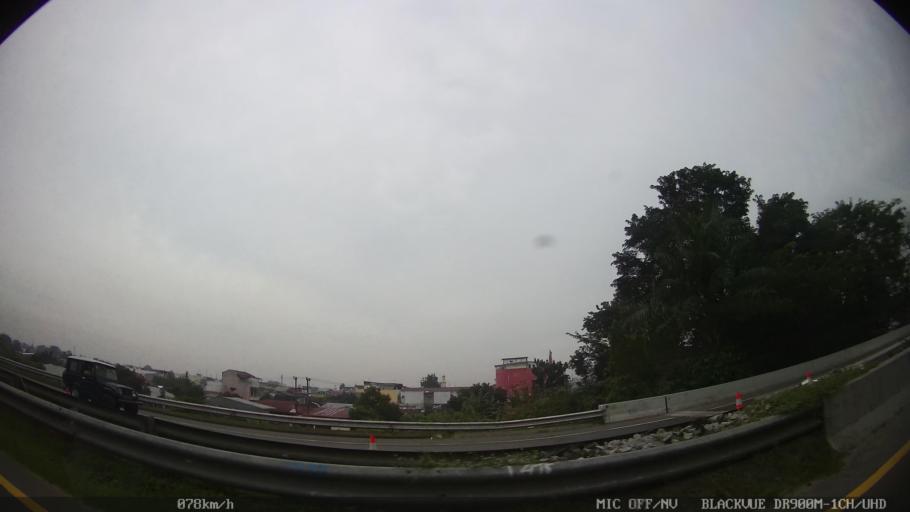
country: ID
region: North Sumatra
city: Medan
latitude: 3.5832
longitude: 98.7242
